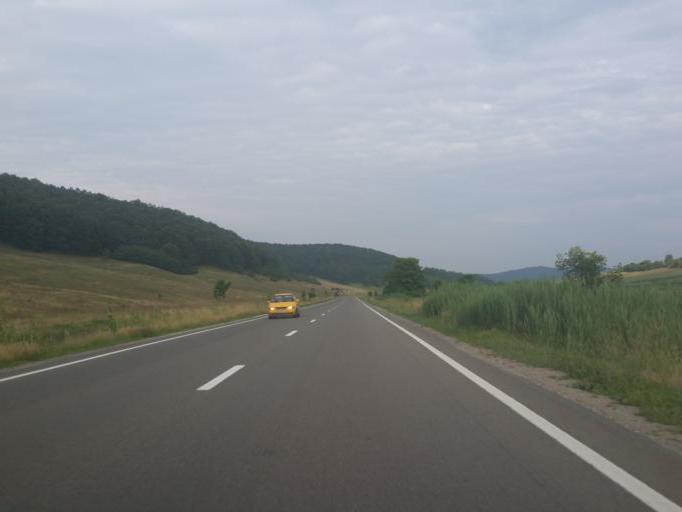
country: RO
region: Salaj
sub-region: Comuna Hida
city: Hida
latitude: 47.0554
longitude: 23.2279
